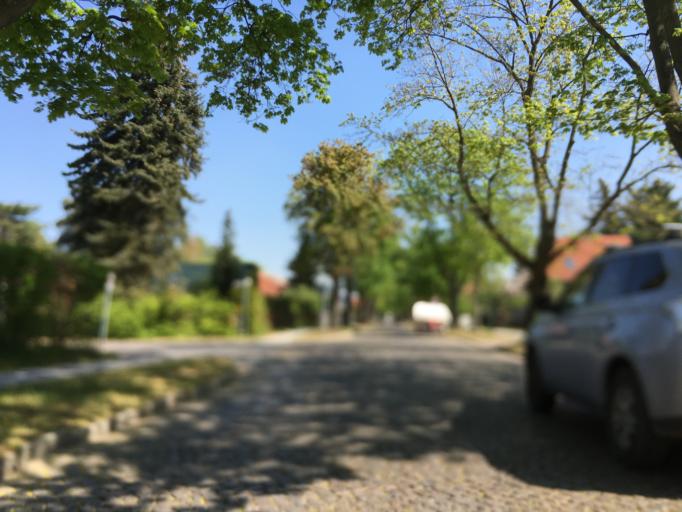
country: DE
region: Berlin
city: Buch
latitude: 52.6516
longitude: 13.5177
